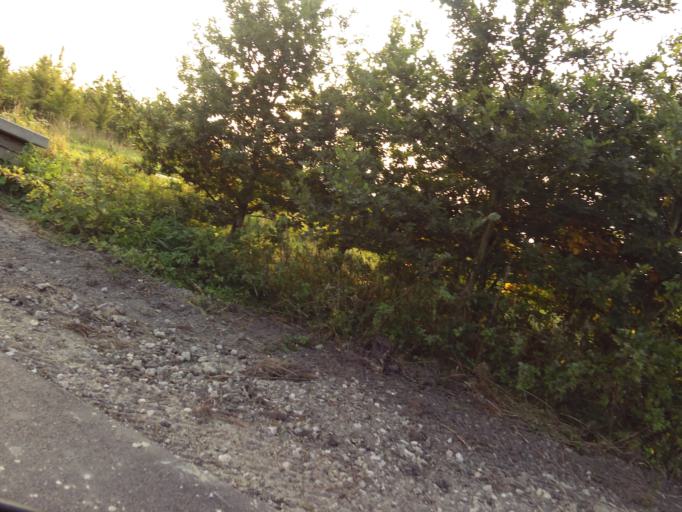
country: NL
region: South Holland
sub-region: Gemeente Rijnwoude
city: Benthuizen
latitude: 52.0686
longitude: 4.5638
